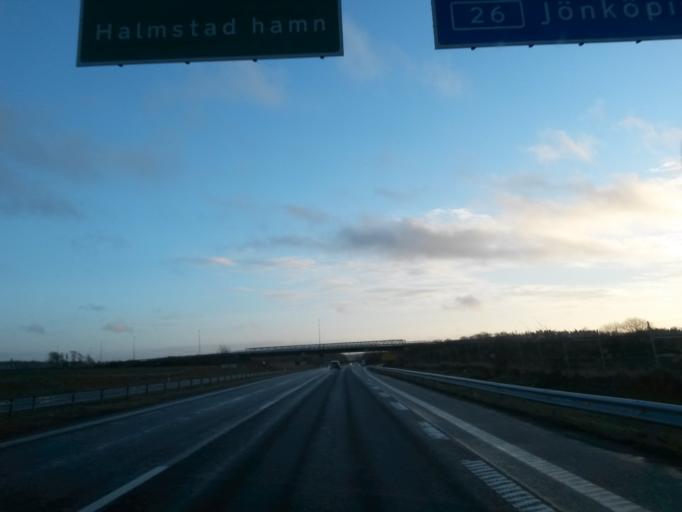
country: SE
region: Halland
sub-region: Halmstads Kommun
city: Halmstad
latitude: 56.7162
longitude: 12.8869
